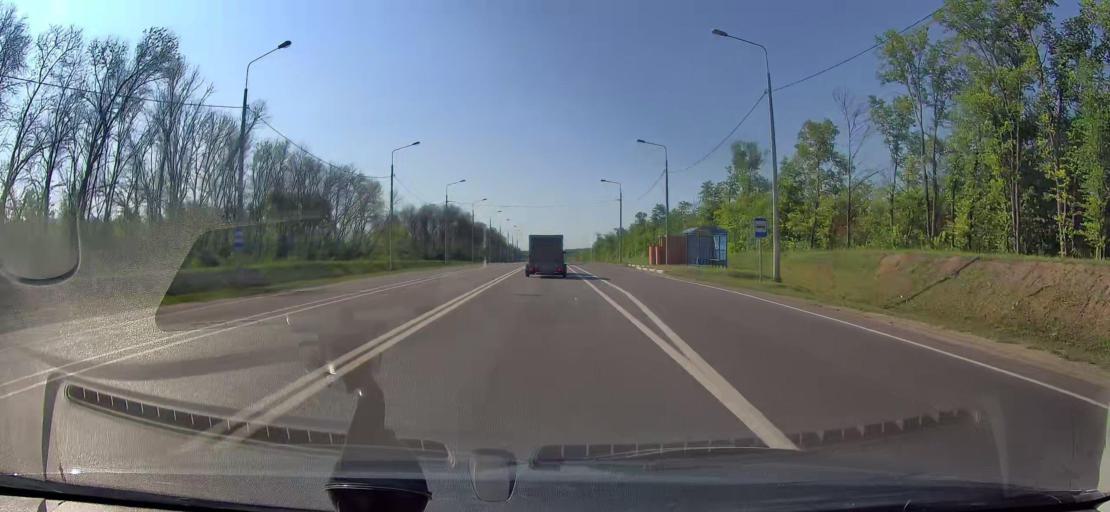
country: RU
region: Orjol
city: Kromy
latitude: 52.6306
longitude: 35.7535
